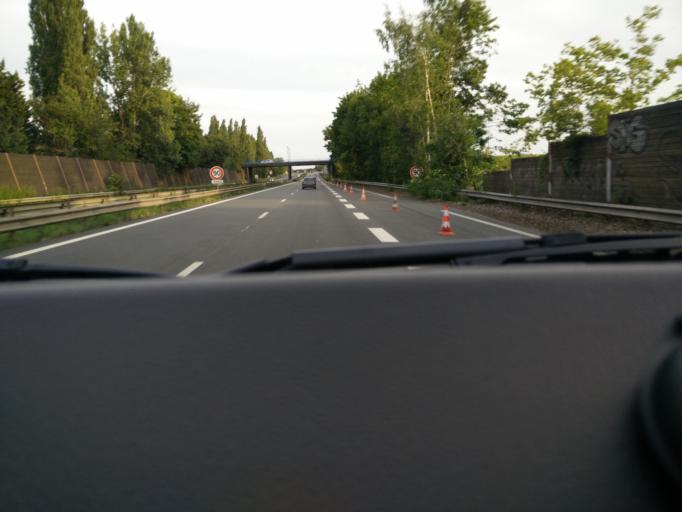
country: FR
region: Nord-Pas-de-Calais
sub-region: Departement du Nord
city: Petite-Foret
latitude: 50.3651
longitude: 3.4841
